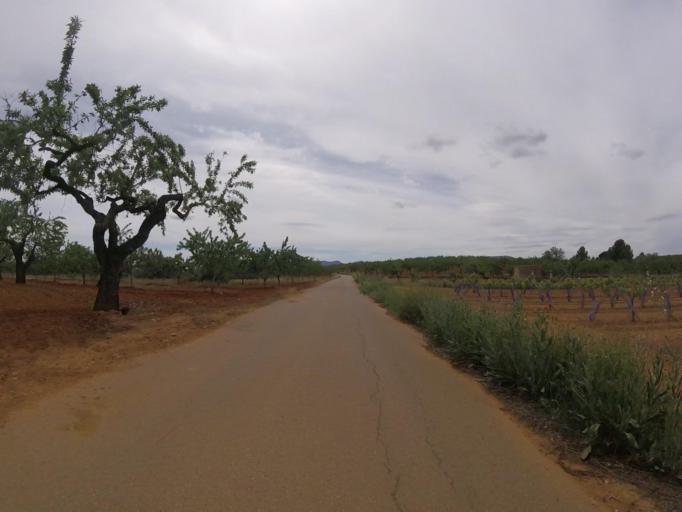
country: ES
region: Valencia
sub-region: Provincia de Castello
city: Benlloch
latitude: 40.1848
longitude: -0.0089
